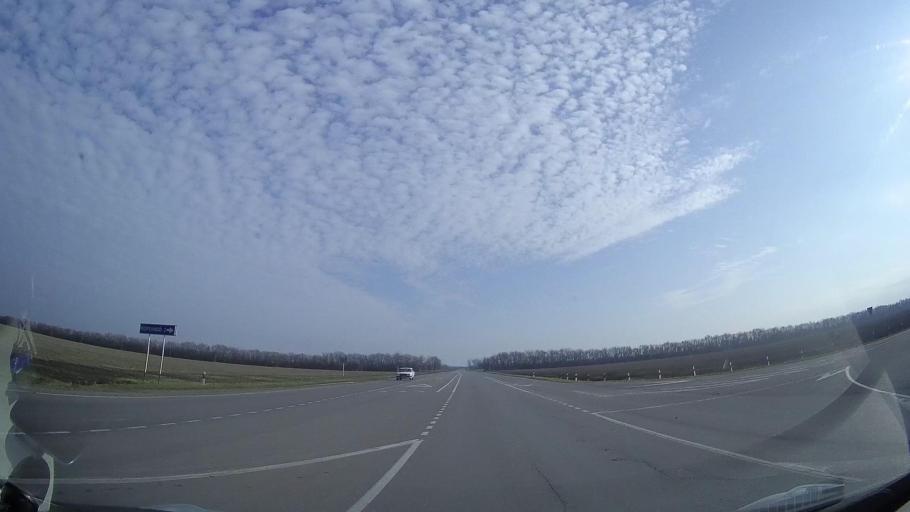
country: RU
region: Rostov
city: Tselina
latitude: 46.5233
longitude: 41.1237
